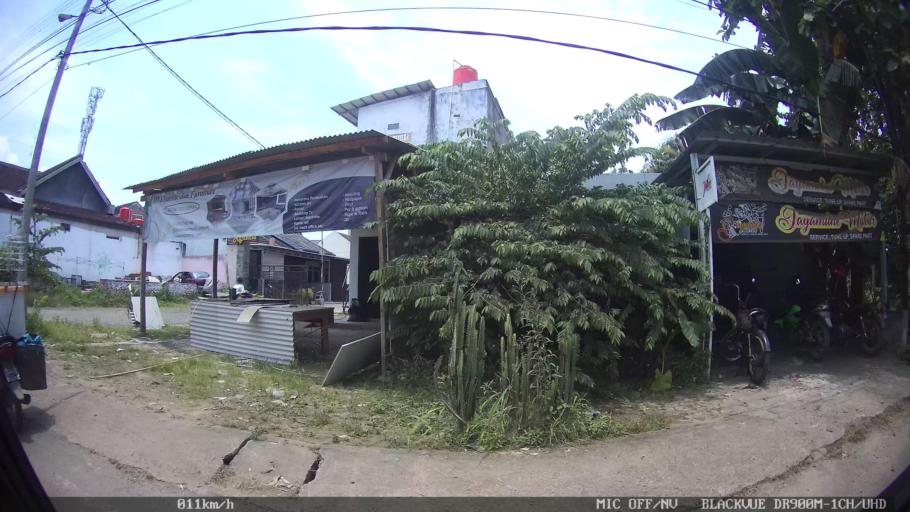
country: ID
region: Lampung
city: Kedaton
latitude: -5.3516
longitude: 105.2403
